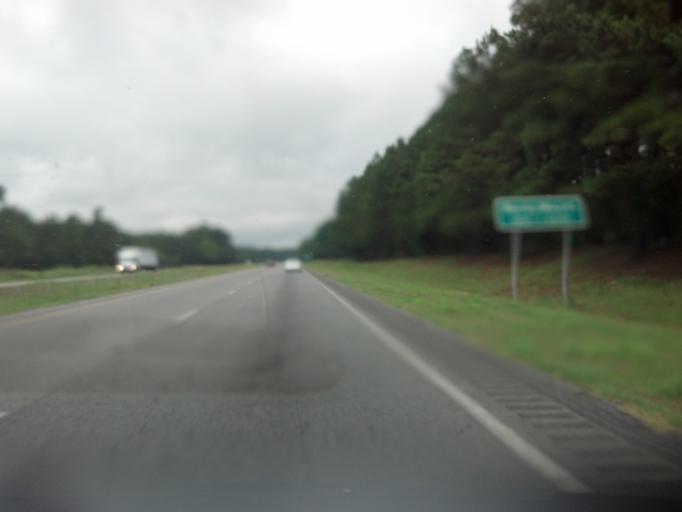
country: US
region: North Carolina
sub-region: Nash County
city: Rocky Mount
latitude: 35.9358
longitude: -77.7331
